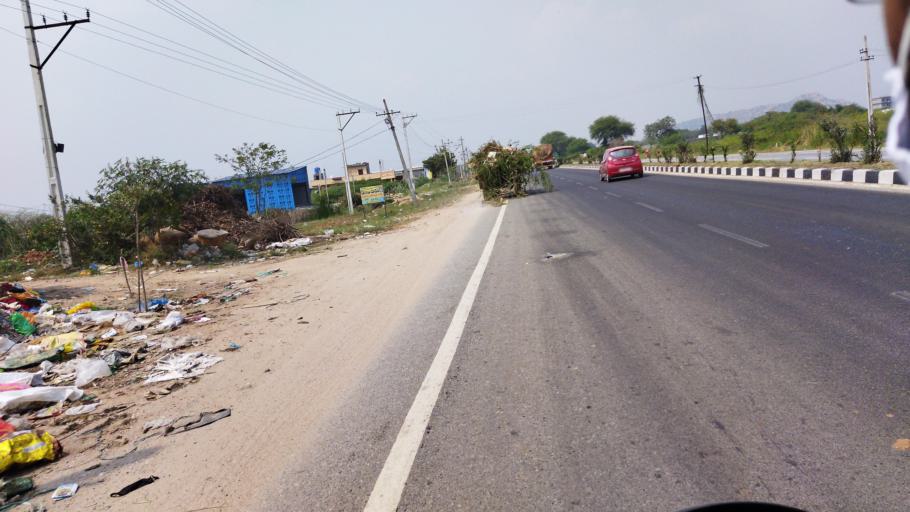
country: IN
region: Telangana
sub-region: Nalgonda
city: Nalgonda
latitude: 17.0753
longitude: 79.2837
